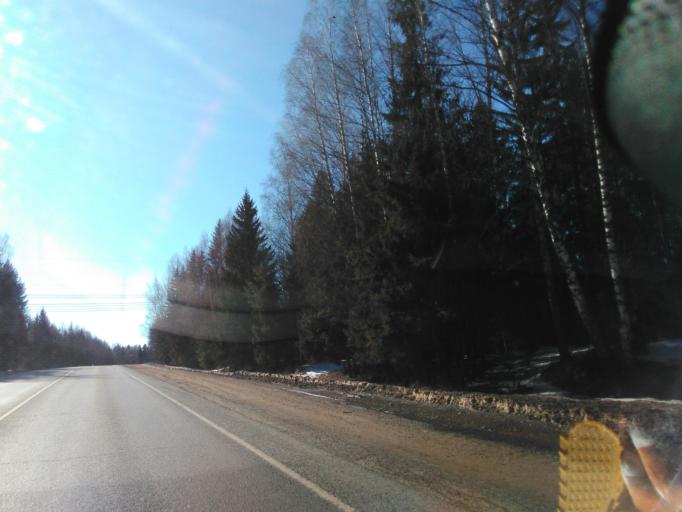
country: RU
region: Moskovskaya
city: Yermolino
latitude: 56.1266
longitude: 37.3448
